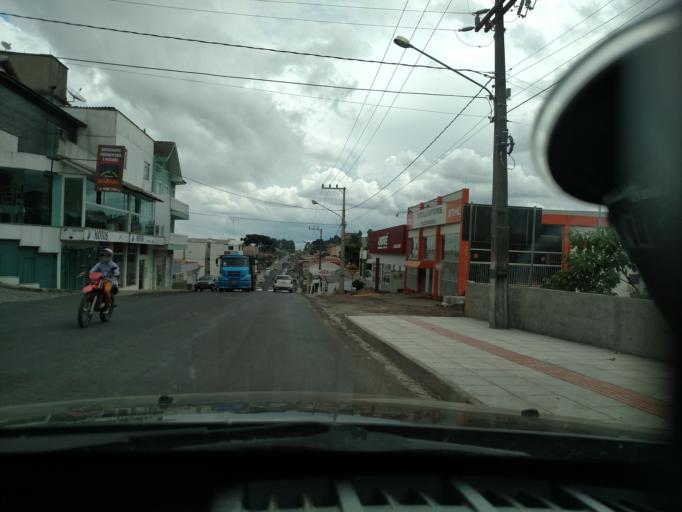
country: BR
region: Santa Catarina
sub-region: Sao Joaquim
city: Sao Joaquim
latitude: -28.2894
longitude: -49.9351
